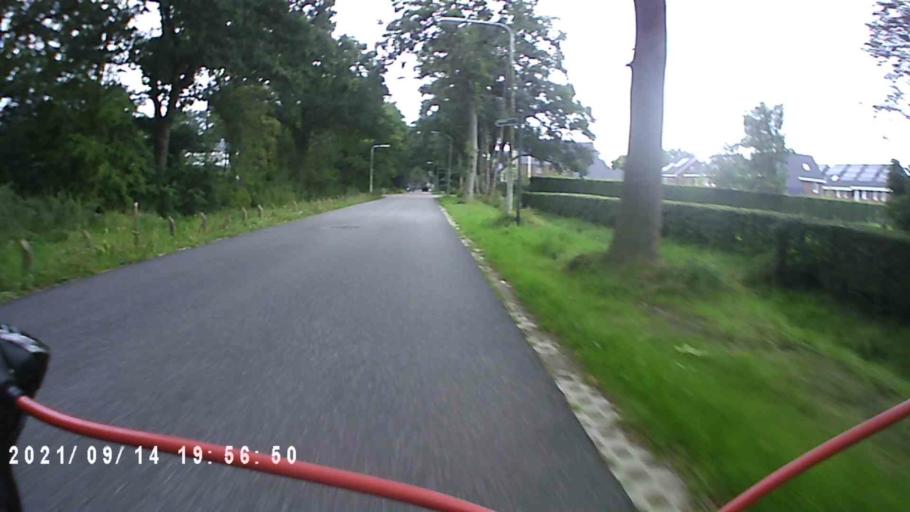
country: NL
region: Groningen
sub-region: Gemeente Haren
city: Haren
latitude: 53.1815
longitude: 6.6075
